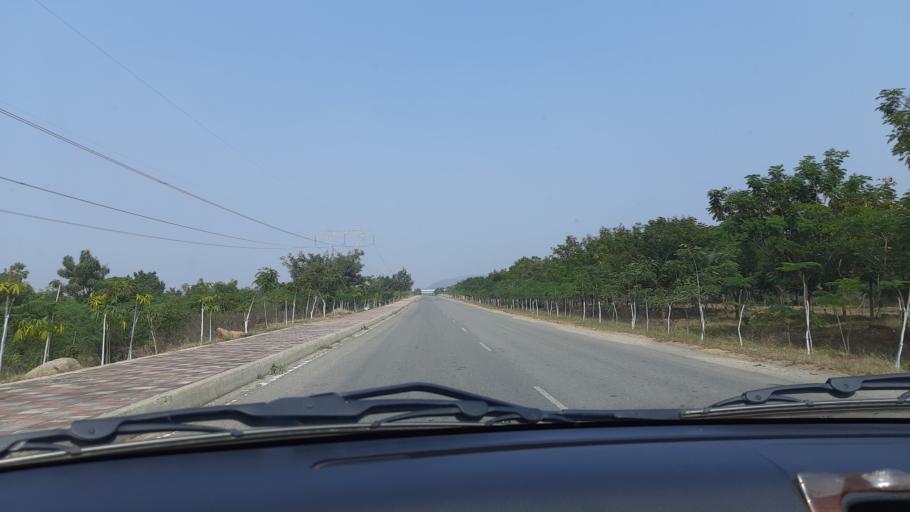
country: IN
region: Telangana
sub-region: Rangareddi
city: Lal Bahadur Nagar
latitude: 17.3012
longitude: 78.6537
